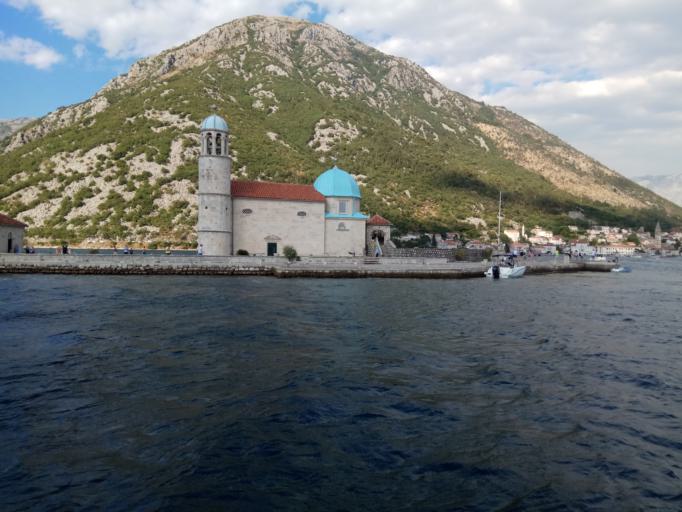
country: ME
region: Kotor
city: Risan
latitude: 42.4865
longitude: 18.6884
